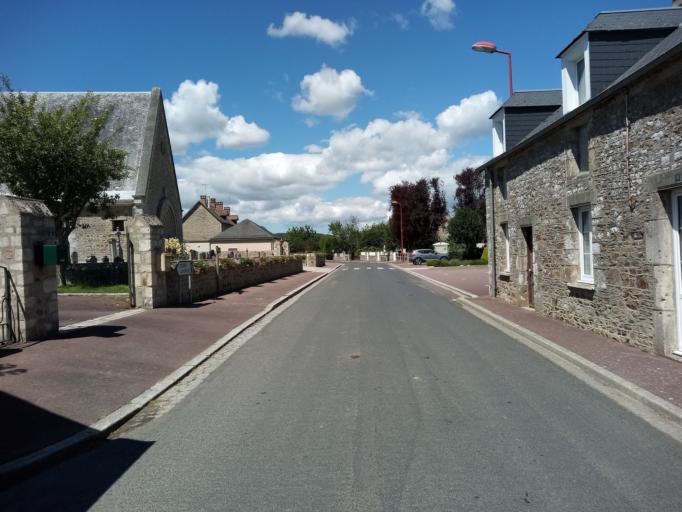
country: FR
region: Lower Normandy
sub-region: Departement de la Manche
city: Periers
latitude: 49.2807
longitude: -1.4248
